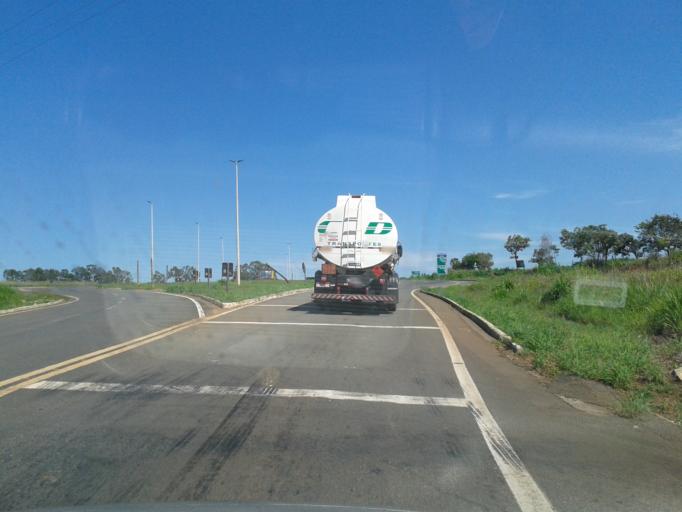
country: BR
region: Goias
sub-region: Bela Vista De Goias
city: Bela Vista de Goias
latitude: -17.0357
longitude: -48.9484
